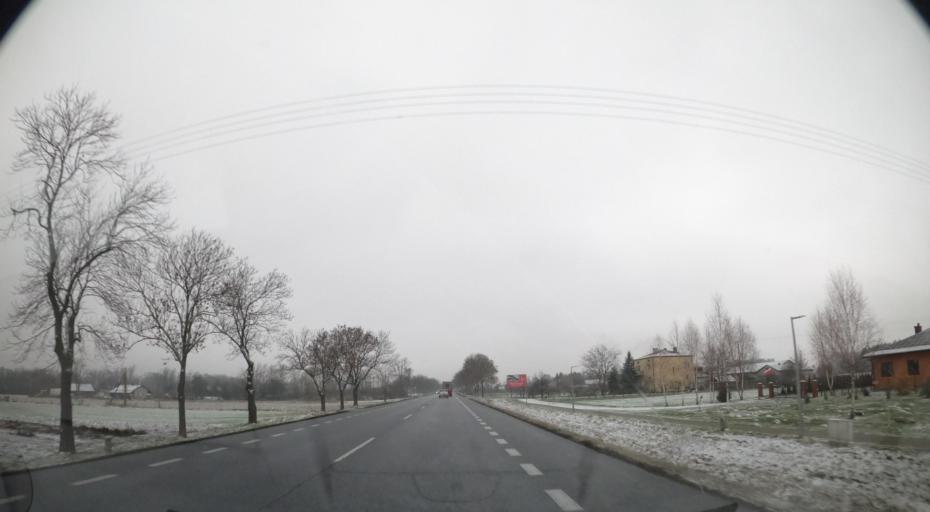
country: PL
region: Masovian Voivodeship
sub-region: Powiat sochaczewski
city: Sochaczew
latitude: 52.2221
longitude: 20.3190
